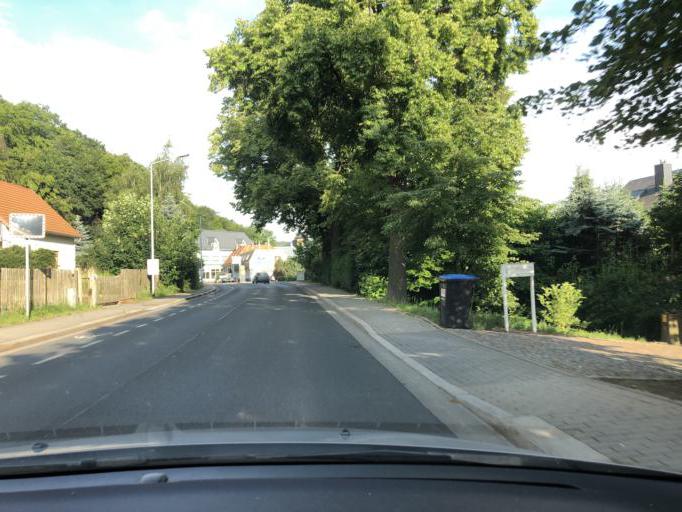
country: DE
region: Saxony
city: Freital
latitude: 50.9890
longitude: 13.6666
